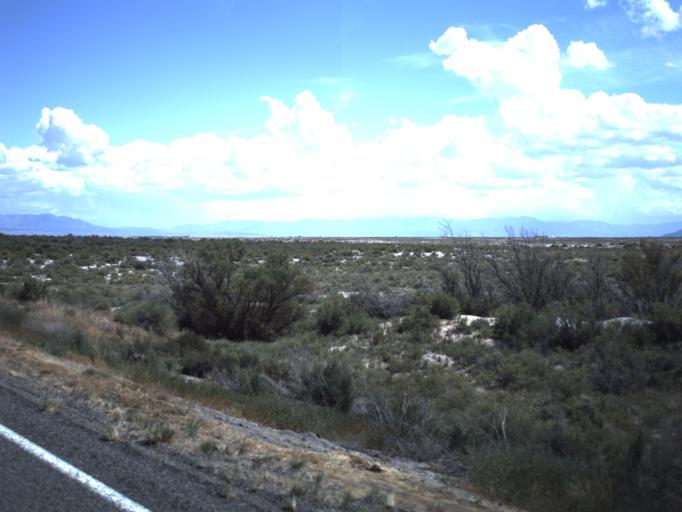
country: US
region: Utah
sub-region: Millard County
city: Delta
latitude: 39.3076
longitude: -112.7895
